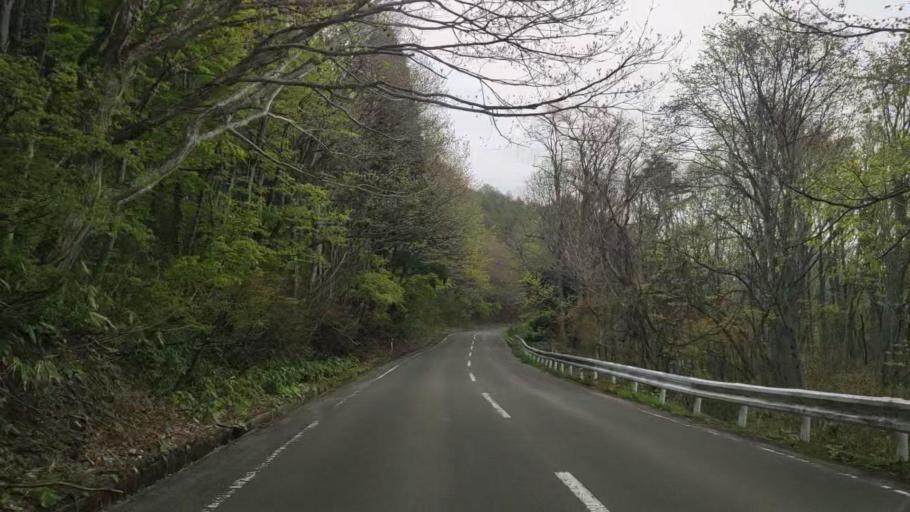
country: JP
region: Aomori
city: Aomori Shi
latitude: 40.7340
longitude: 140.8391
